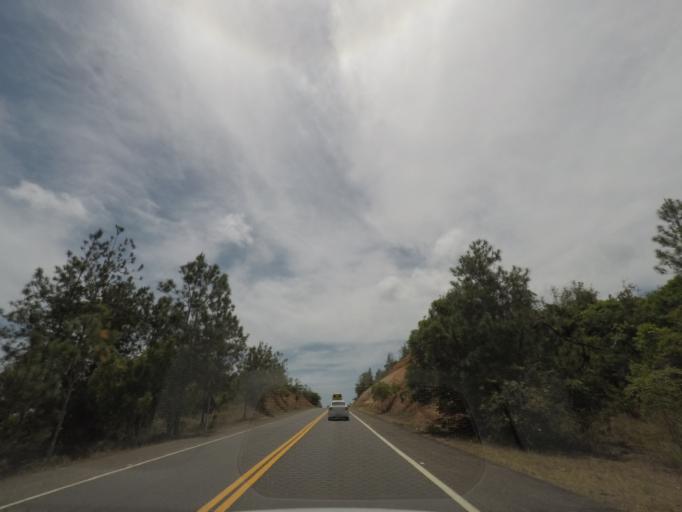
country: BR
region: Bahia
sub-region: Conde
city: Conde
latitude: -11.9798
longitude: -37.6757
